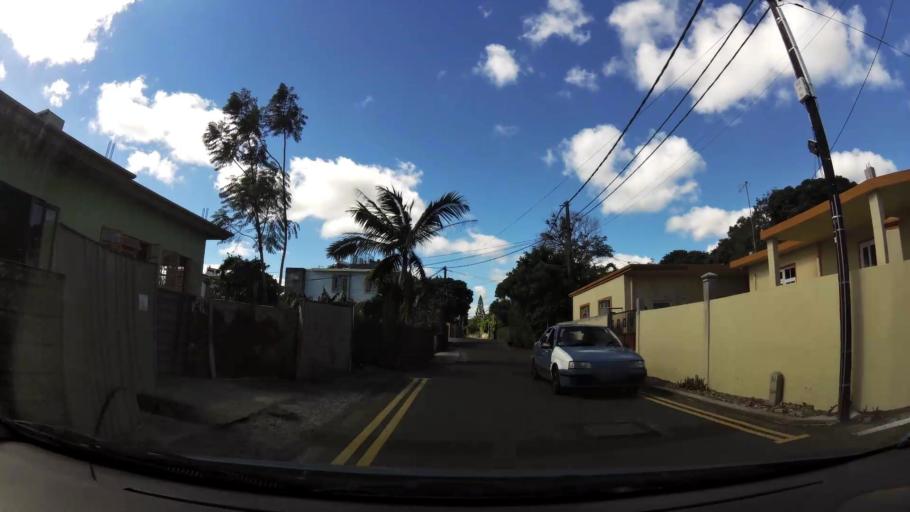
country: MU
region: Plaines Wilhems
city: Vacoas
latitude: -20.3013
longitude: 57.4812
